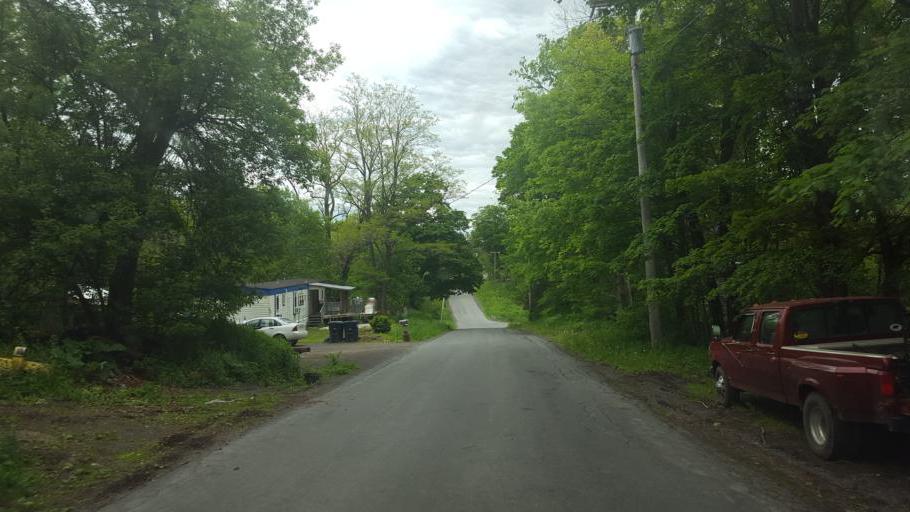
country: US
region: New York
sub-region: Otsego County
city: Richfield Springs
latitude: 42.8574
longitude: -75.0559
